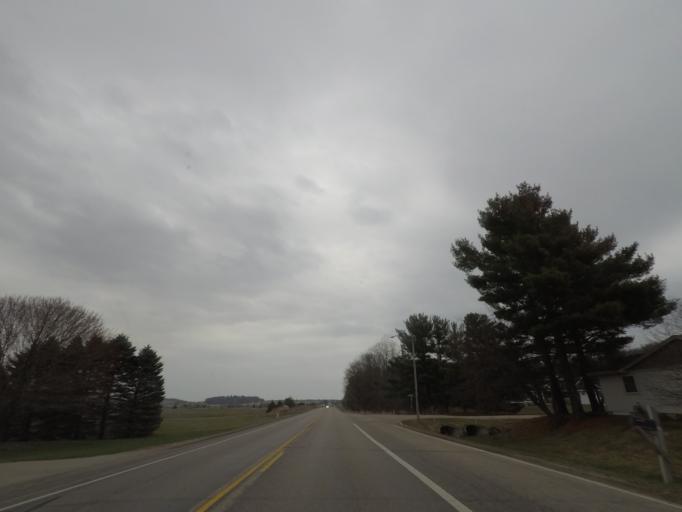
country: US
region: Wisconsin
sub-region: Dane County
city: Middleton
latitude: 43.1111
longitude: -89.5465
